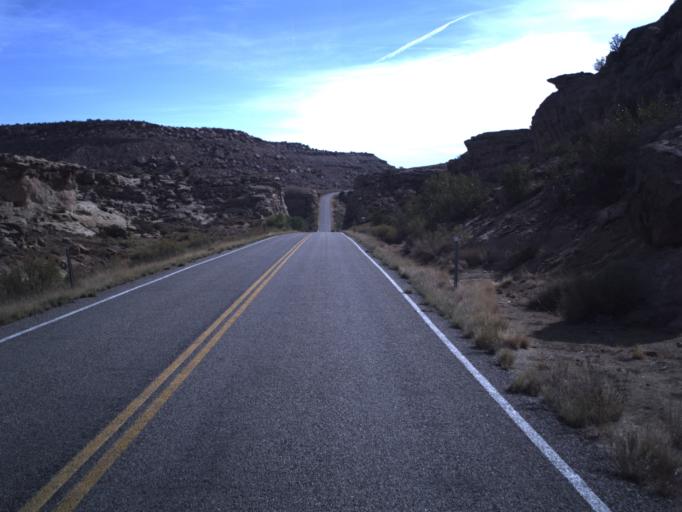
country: US
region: Utah
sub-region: San Juan County
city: Blanding
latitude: 37.4183
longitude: -109.4487
